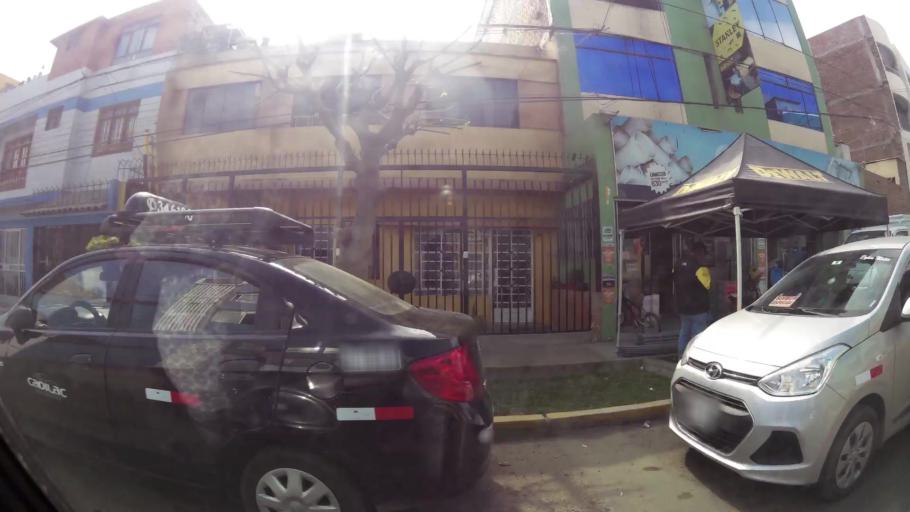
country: PE
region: La Libertad
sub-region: Provincia de Trujillo
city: Trujillo
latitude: -8.1137
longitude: -79.0159
